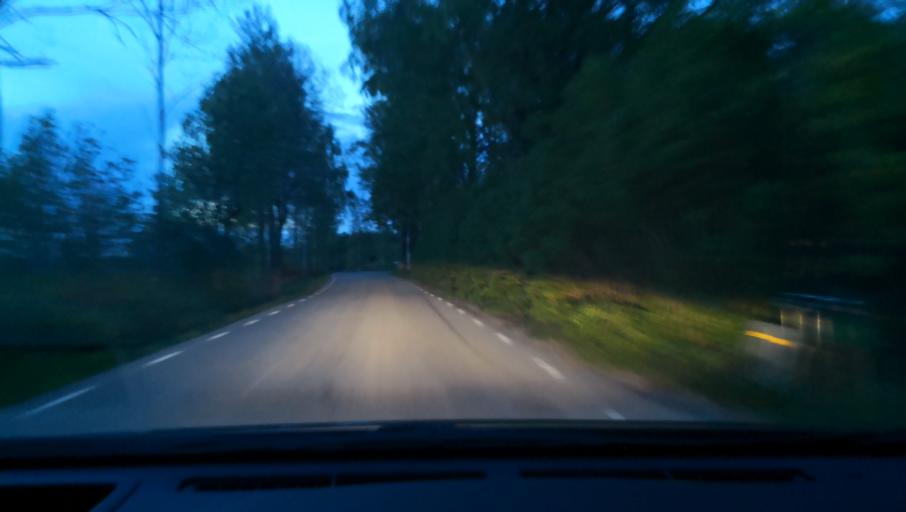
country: SE
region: OErebro
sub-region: Orebro Kommun
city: Vintrosa
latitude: 59.1628
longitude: 15.0031
